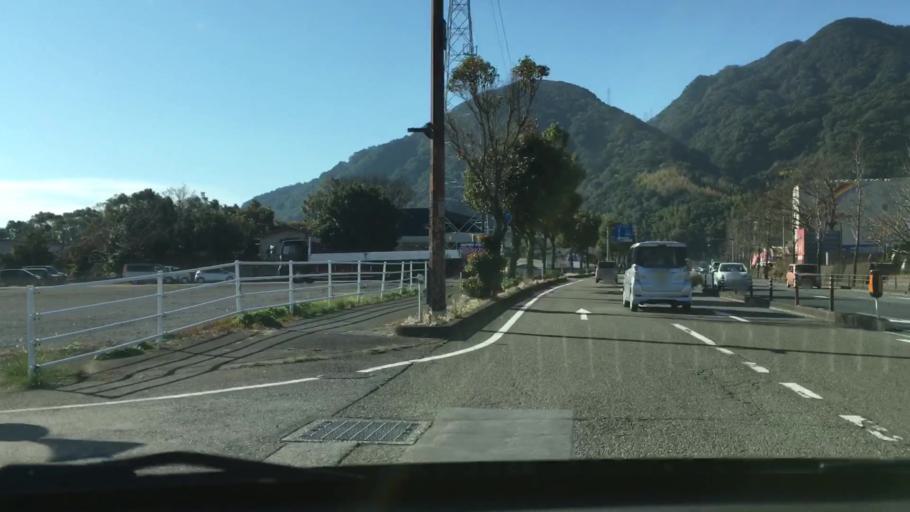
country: JP
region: Kagoshima
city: Kajiki
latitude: 31.7079
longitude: 130.6147
